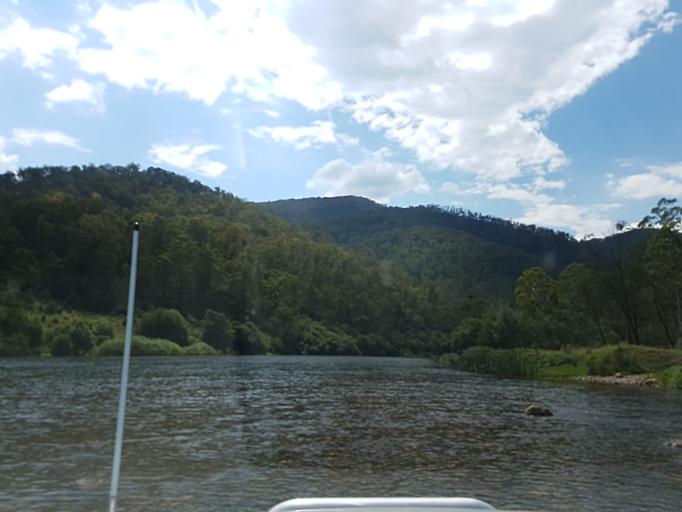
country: AU
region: Victoria
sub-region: East Gippsland
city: Lakes Entrance
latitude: -37.3941
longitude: 148.3337
